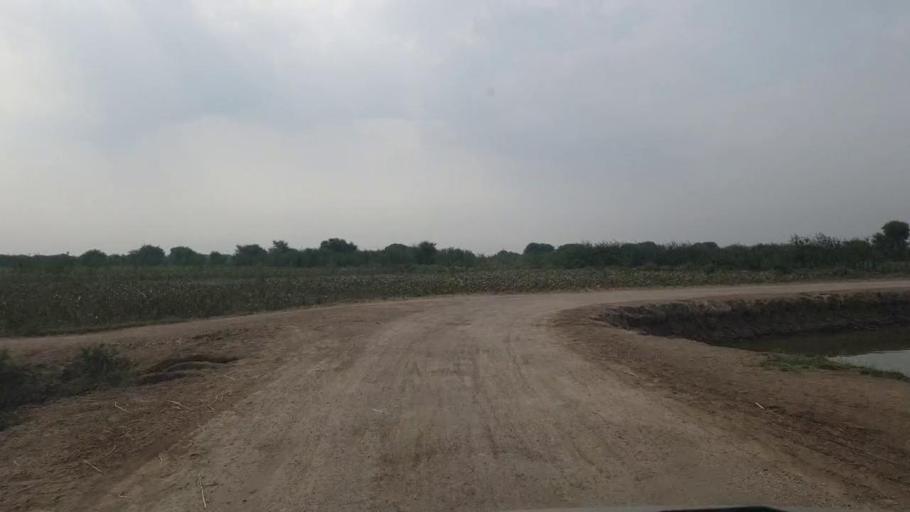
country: PK
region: Sindh
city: Talhar
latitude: 24.8627
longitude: 68.8342
